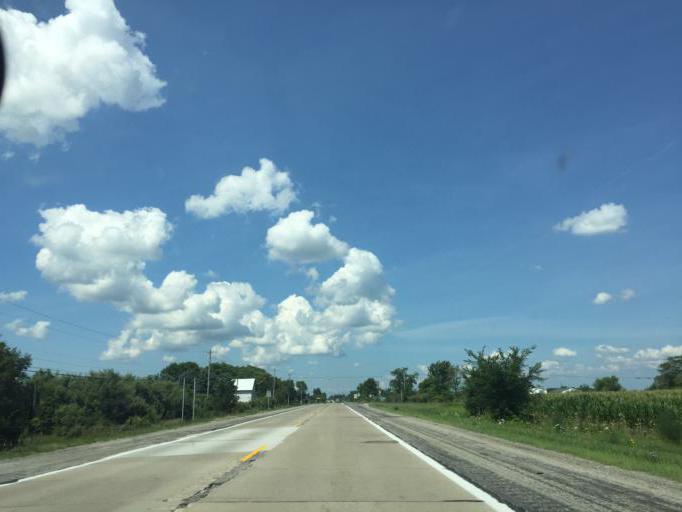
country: US
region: Ohio
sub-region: Lucas County
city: Sylvania
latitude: 41.7964
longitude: -83.7337
